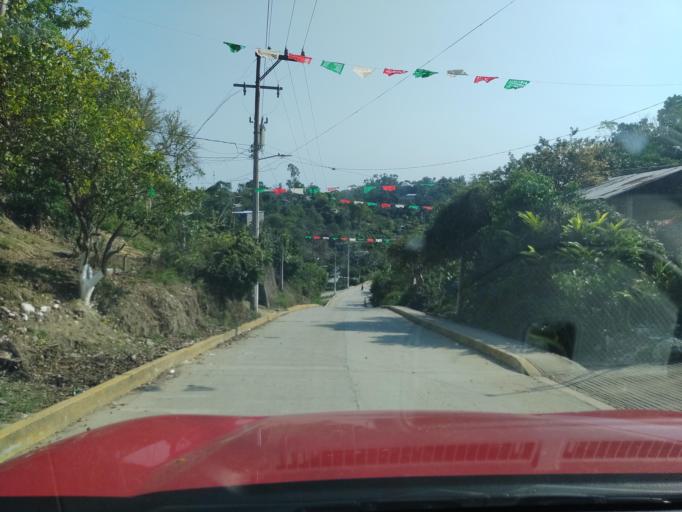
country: MX
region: Veracruz
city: Agua Dulce
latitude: 20.3505
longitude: -97.1758
